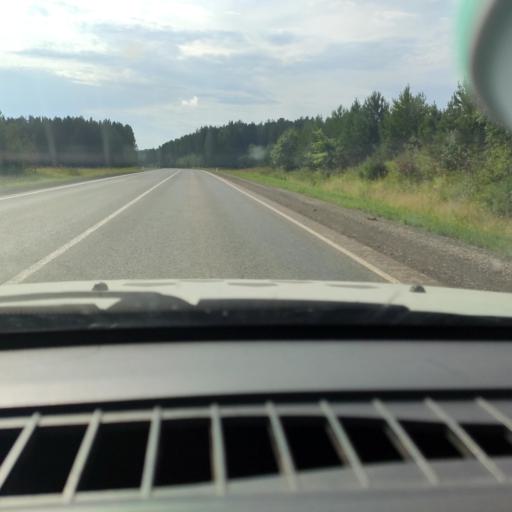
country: RU
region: Perm
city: Siva
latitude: 58.4106
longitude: 54.4707
